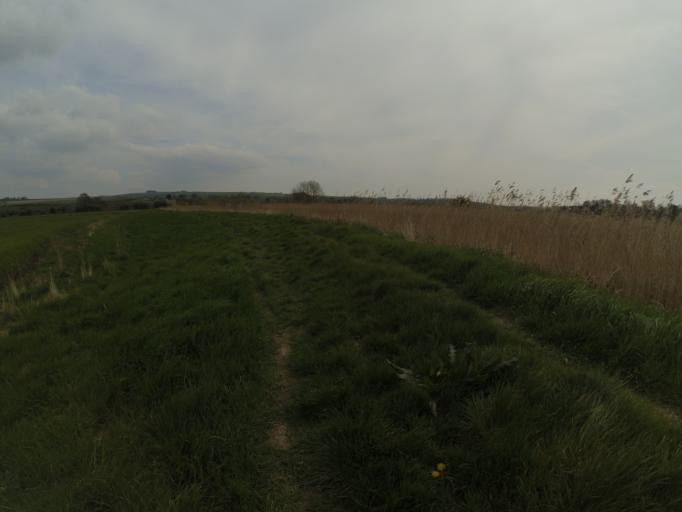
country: GB
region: England
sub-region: West Sussex
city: Arundel
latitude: 50.8744
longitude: -0.5401
